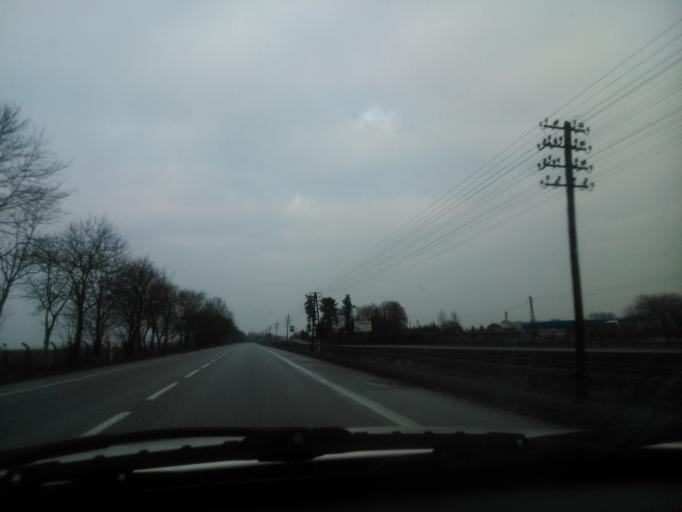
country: PL
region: Kujawsko-Pomorskie
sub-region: Powiat torunski
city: Lysomice
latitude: 53.0736
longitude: 18.6179
